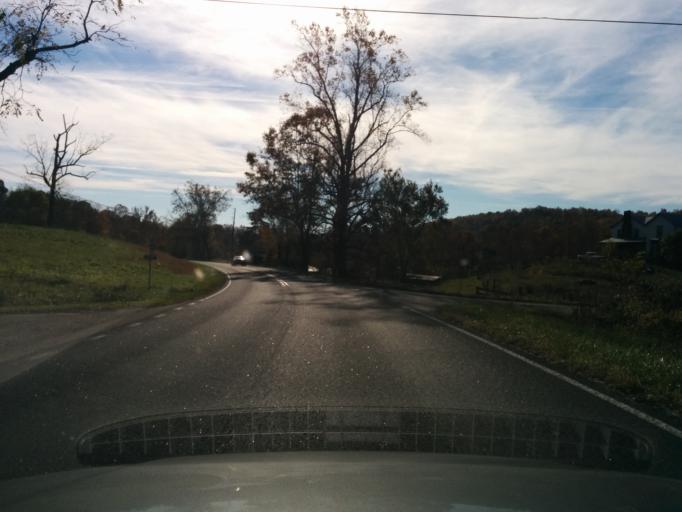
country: US
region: Virginia
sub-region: City of Lexington
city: Lexington
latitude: 37.8225
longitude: -79.4958
